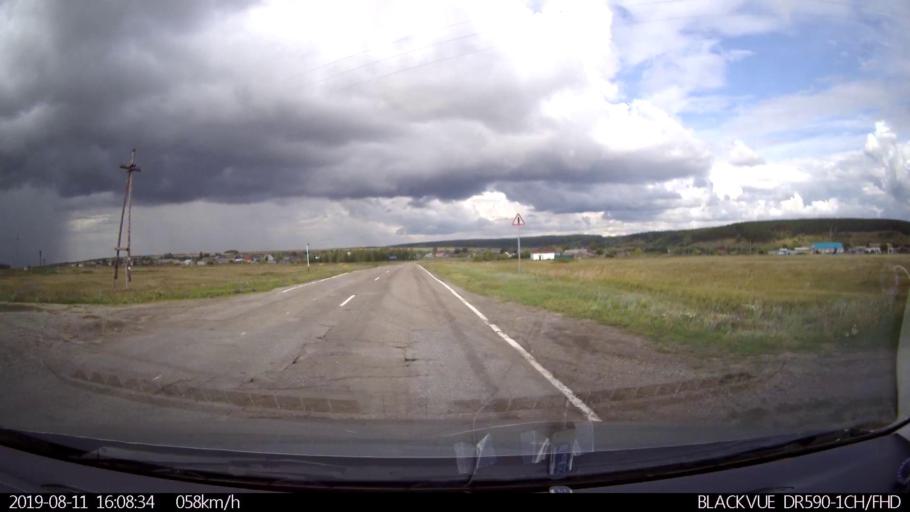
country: RU
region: Ulyanovsk
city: Ignatovka
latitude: 53.9858
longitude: 47.6485
